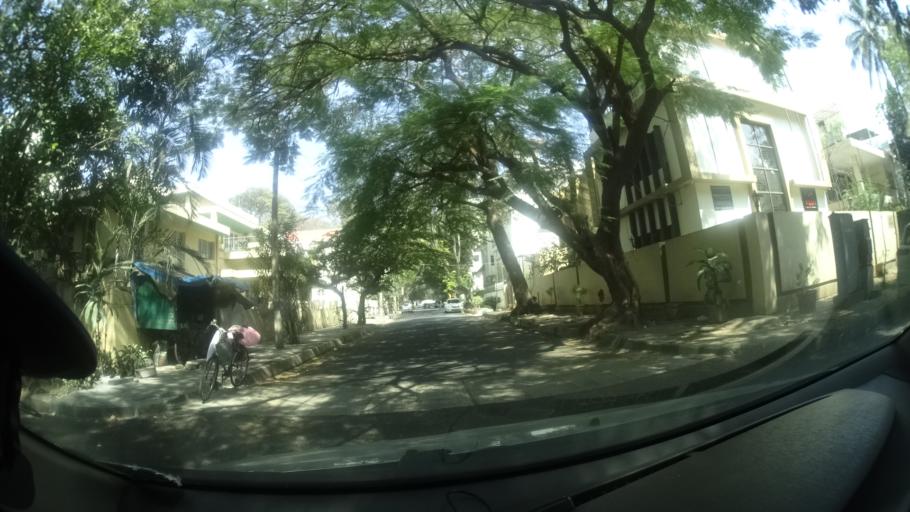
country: IN
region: Karnataka
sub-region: Bangalore Urban
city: Bangalore
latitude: 13.0124
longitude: 77.5784
